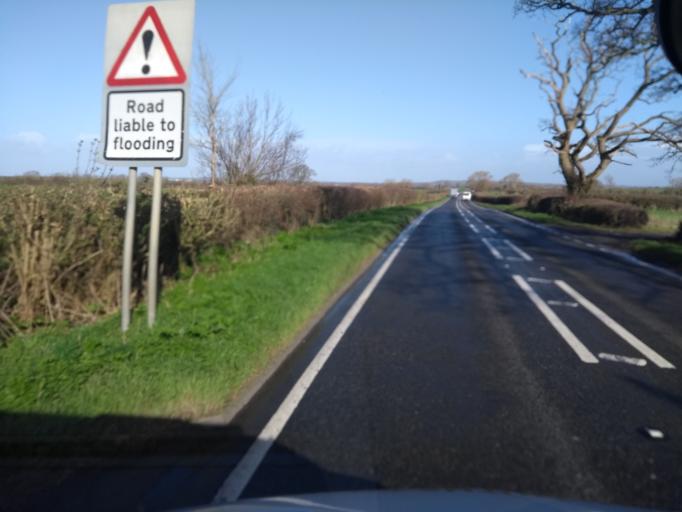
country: GB
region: England
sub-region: Somerset
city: Ilchester
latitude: 50.9790
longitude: -2.6738
